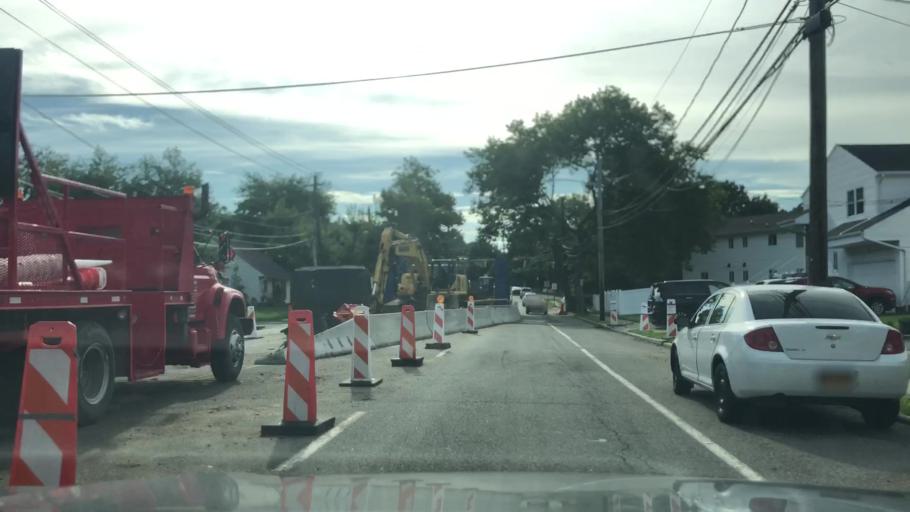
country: US
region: New York
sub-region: Nassau County
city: North Merrick
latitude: 40.6946
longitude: -73.5732
